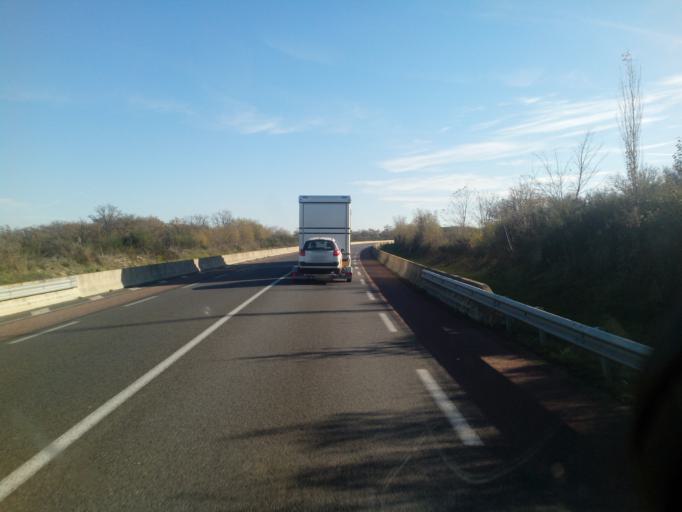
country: FR
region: Limousin
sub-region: Departement de la Haute-Vienne
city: Bellac
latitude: 46.1362
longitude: 1.0621
